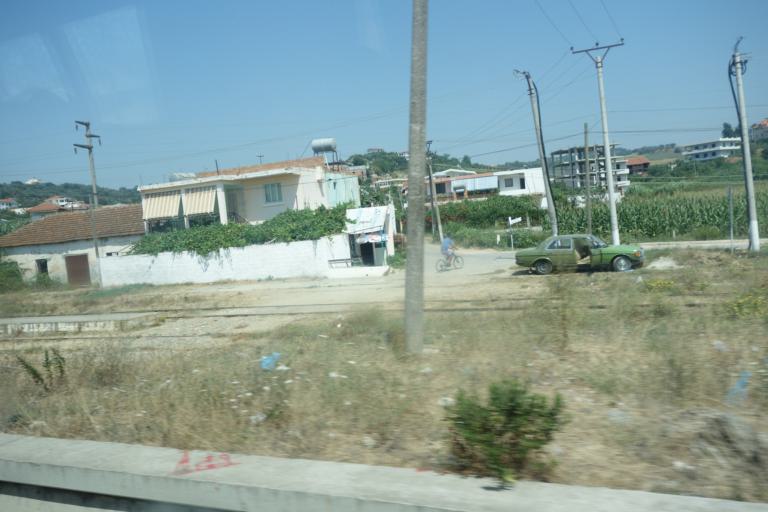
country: AL
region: Tirane
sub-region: Rrethi i Kavajes
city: Golem
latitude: 41.2560
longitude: 19.5266
